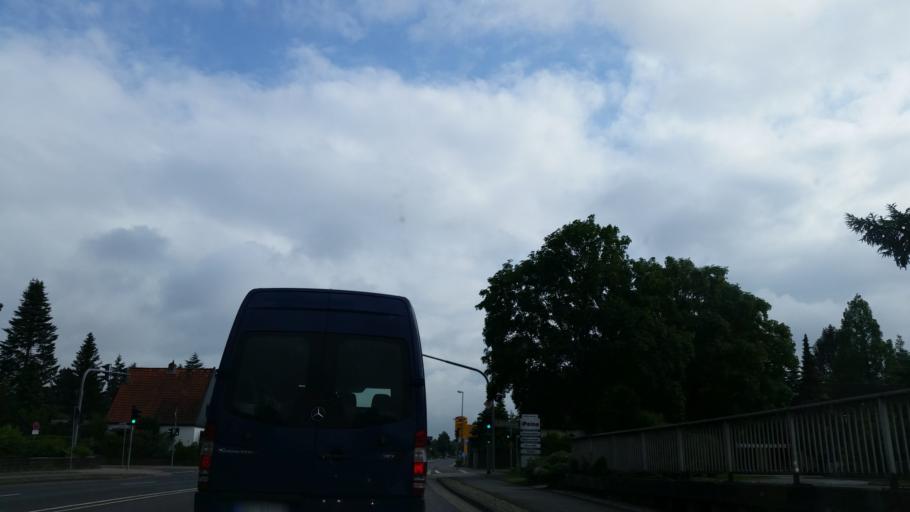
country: DE
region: Lower Saxony
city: Peine
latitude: 52.3350
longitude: 10.2371
